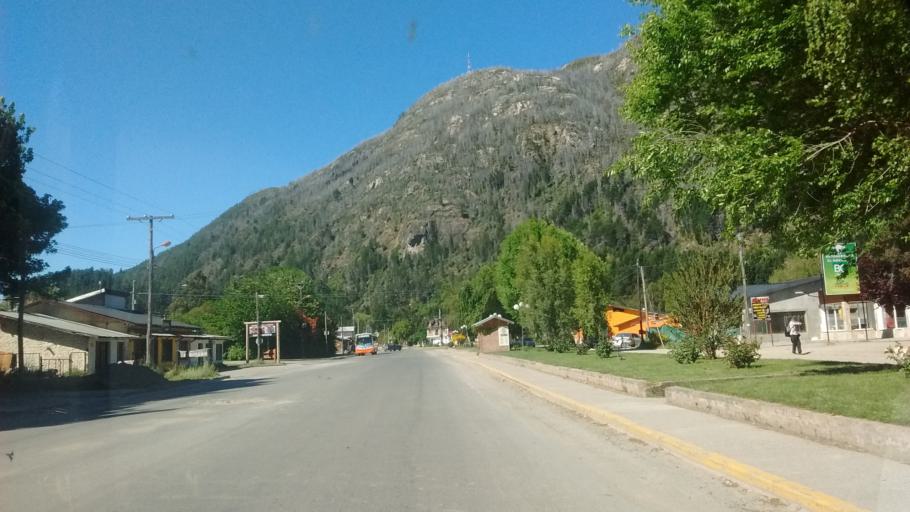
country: AR
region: Chubut
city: Lago Puelo
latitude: -42.0596
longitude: -71.5998
